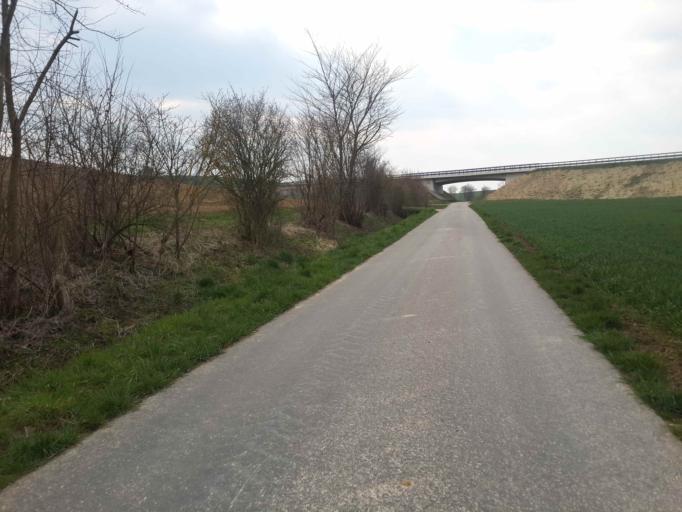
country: DE
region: Baden-Wuerttemberg
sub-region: Regierungsbezirk Stuttgart
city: Ittlingen
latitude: 49.1638
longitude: 8.9343
